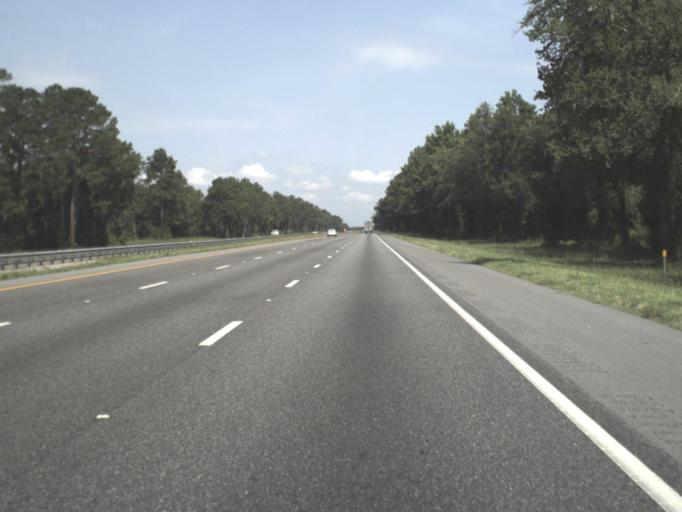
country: US
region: Florida
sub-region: Hamilton County
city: Jasper
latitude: 30.4660
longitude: -82.9612
